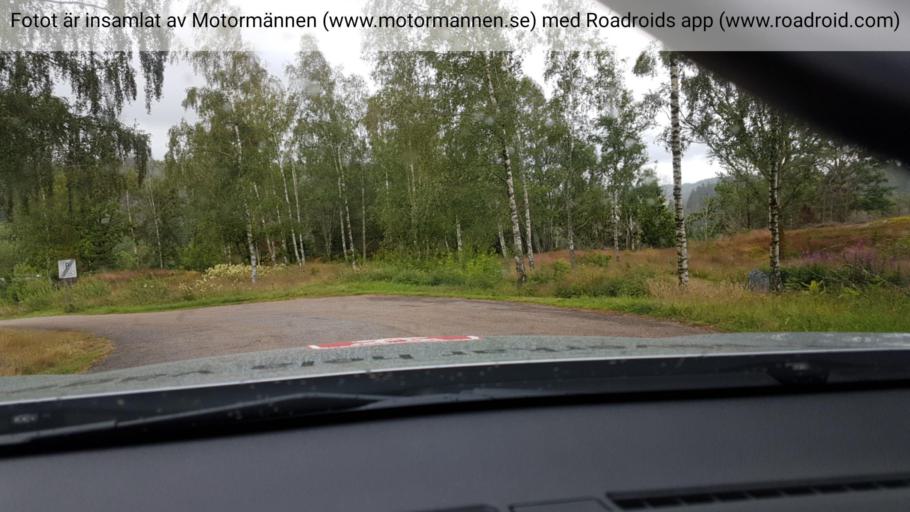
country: SE
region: Vaestra Goetaland
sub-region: Tanums Kommun
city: Tanumshede
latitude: 58.5862
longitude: 11.4489
